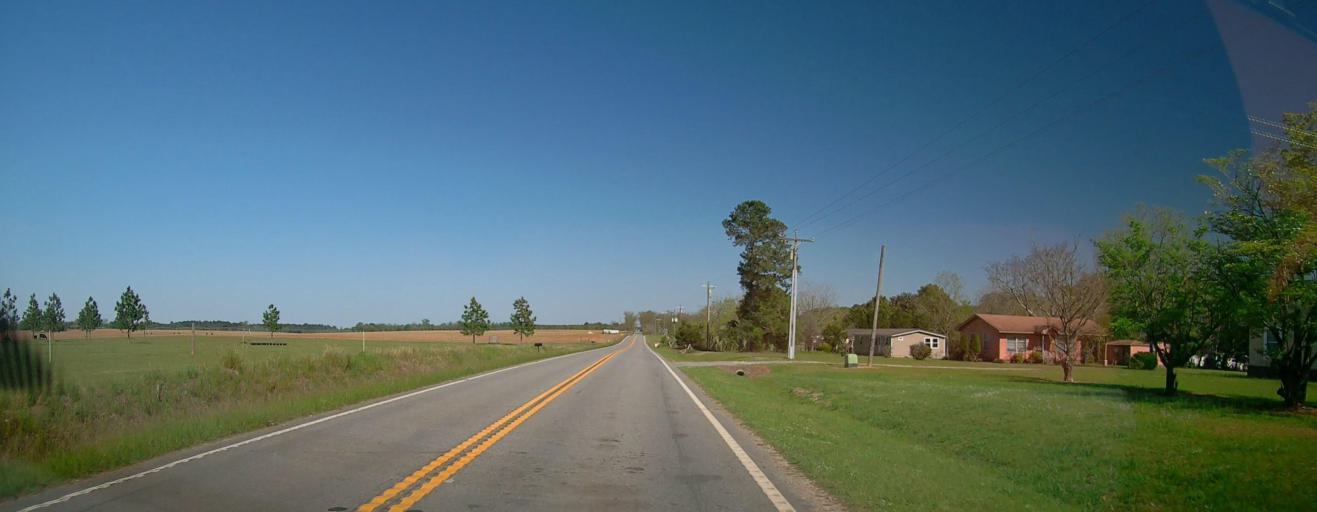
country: US
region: Georgia
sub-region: Dooly County
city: Unadilla
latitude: 32.2603
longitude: -83.7127
